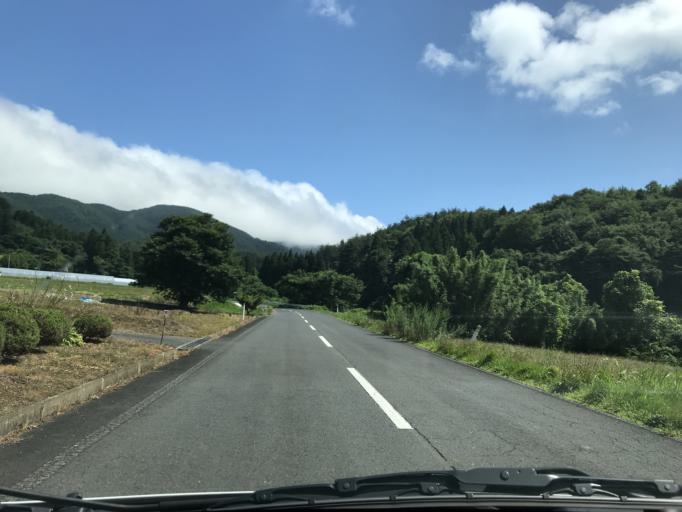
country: JP
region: Iwate
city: Ofunato
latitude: 39.0010
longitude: 141.4264
